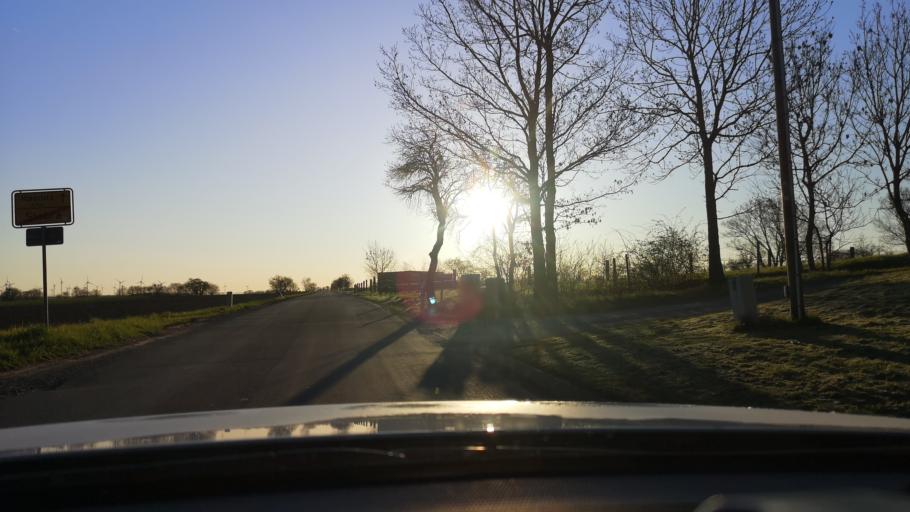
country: DE
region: Thuringia
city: Lehesten
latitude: 51.0041
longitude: 11.5670
